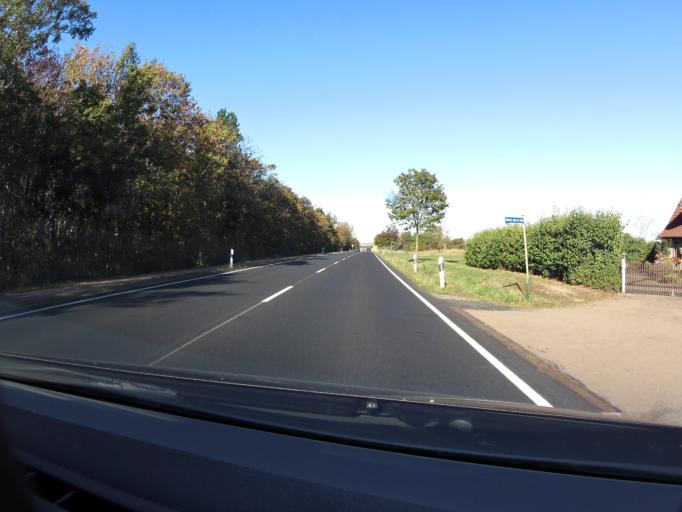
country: DE
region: Saxony-Anhalt
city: Ditfurt
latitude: 51.8005
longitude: 11.1878
